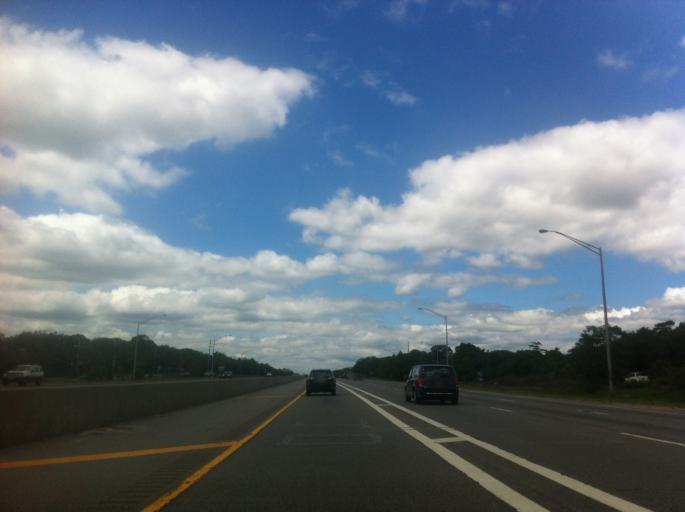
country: US
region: New York
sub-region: Suffolk County
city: Farmingville
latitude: 40.8234
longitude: -73.0218
